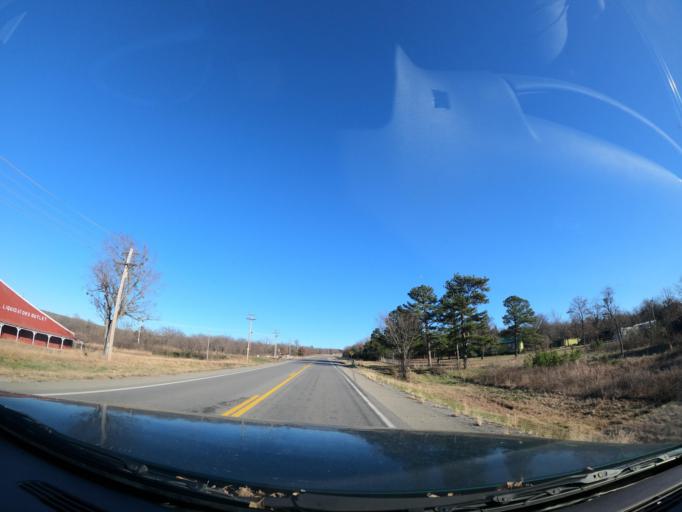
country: US
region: Oklahoma
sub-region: Pittsburg County
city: Longtown
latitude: 35.2392
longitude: -95.4785
